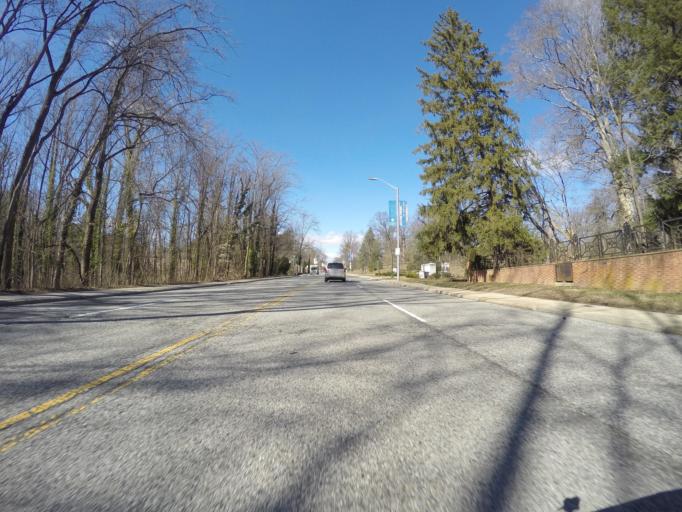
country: US
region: Maryland
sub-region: Baltimore County
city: Towson
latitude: 39.3481
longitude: -76.6226
